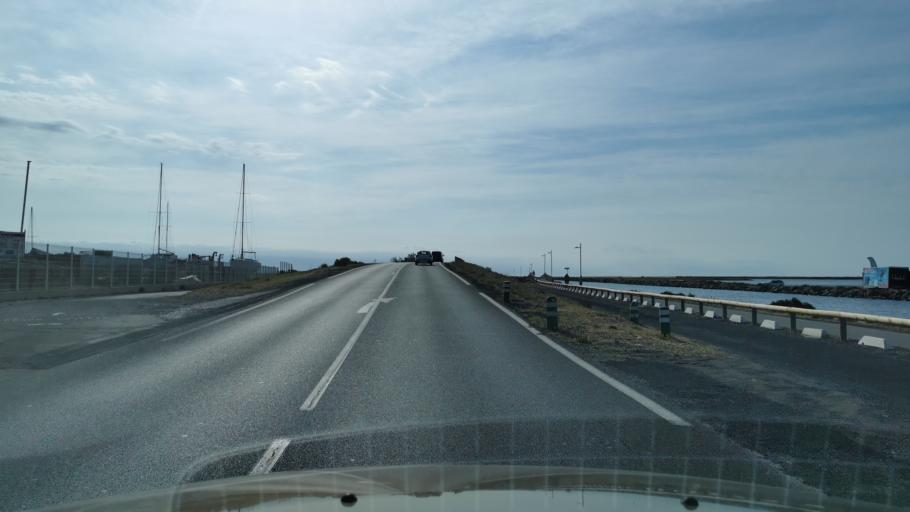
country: FR
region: Languedoc-Roussillon
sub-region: Departement de l'Aude
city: Gruissan
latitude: 43.1009
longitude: 3.0958
